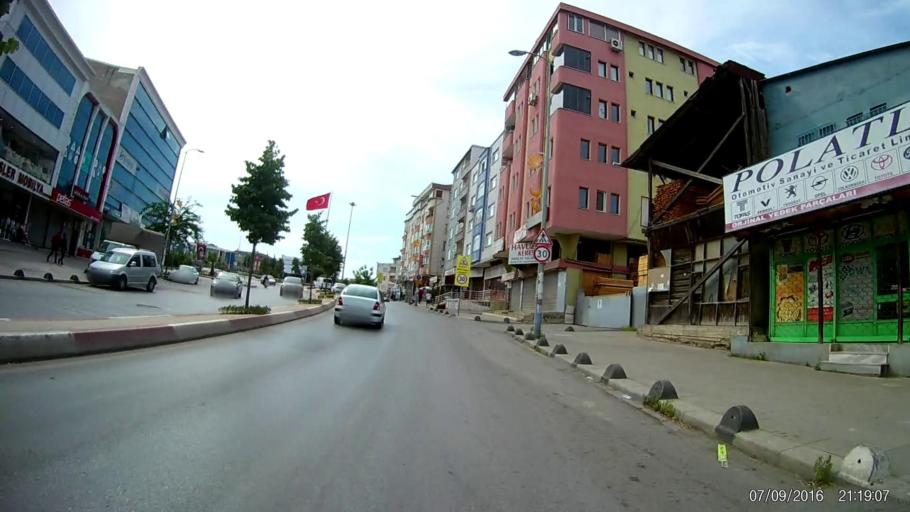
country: TR
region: Istanbul
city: Sultanbeyli
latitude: 40.9662
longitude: 29.2752
